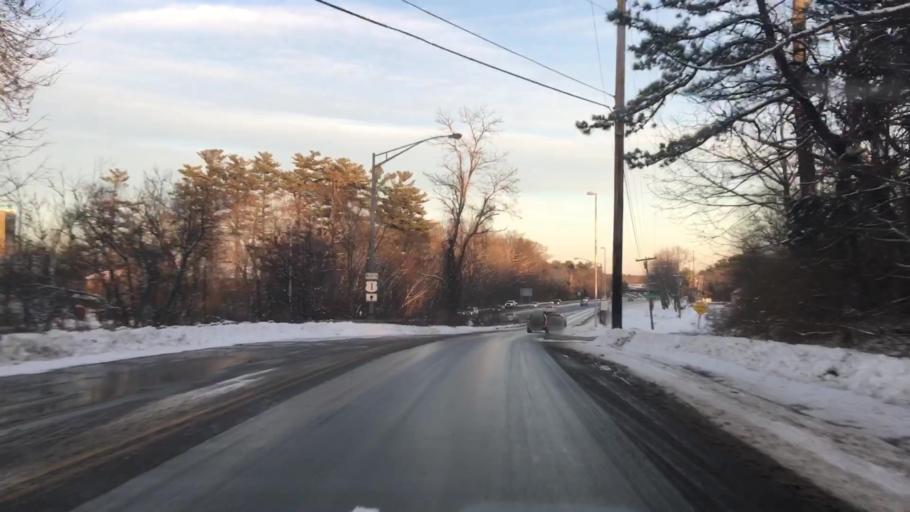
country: US
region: Maine
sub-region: Cumberland County
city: Brunswick
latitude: 43.9181
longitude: -69.9641
